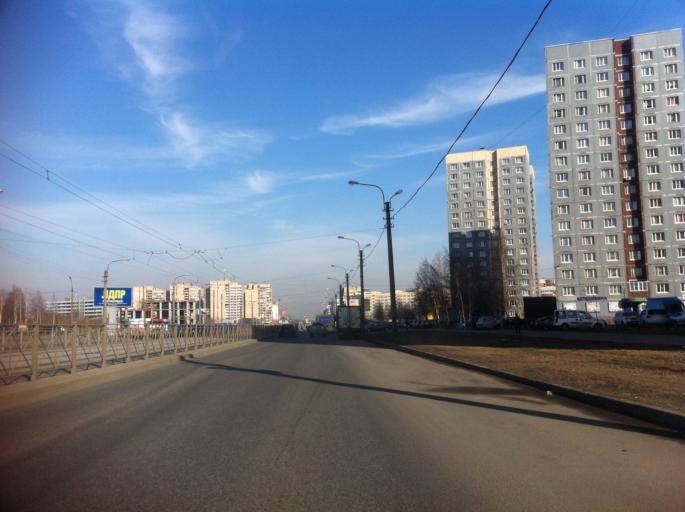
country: RU
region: St.-Petersburg
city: Dachnoye
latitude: 59.8597
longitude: 30.2231
